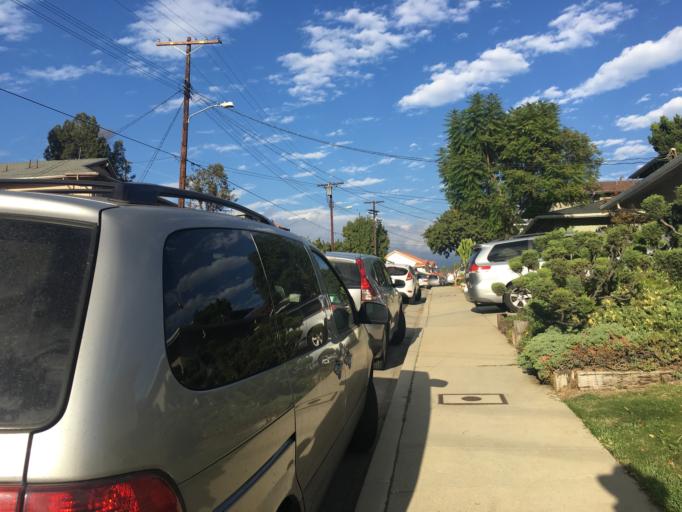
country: US
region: California
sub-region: Los Angeles County
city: Glendale
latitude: 34.1330
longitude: -118.2266
